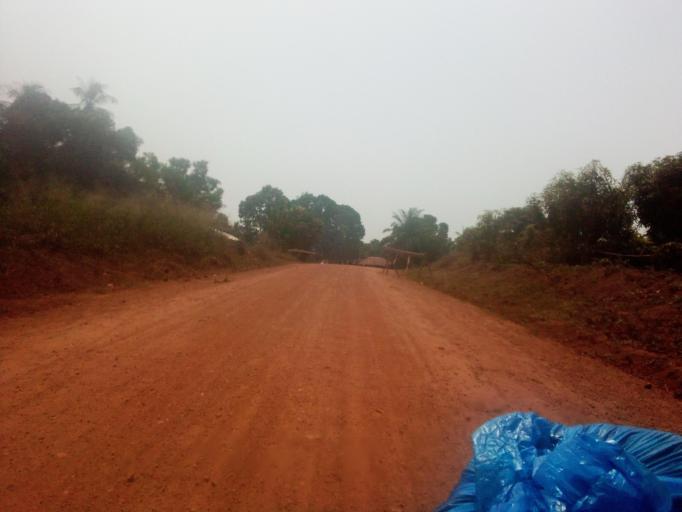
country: SL
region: Southern Province
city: Sumbuya
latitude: 7.6629
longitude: -11.9904
